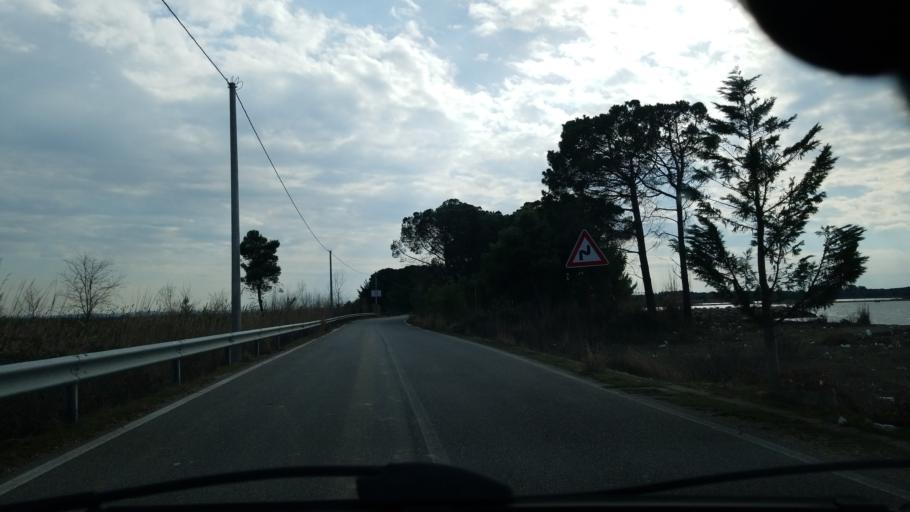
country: AL
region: Lezhe
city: Shengjin
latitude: 41.7699
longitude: 19.6003
